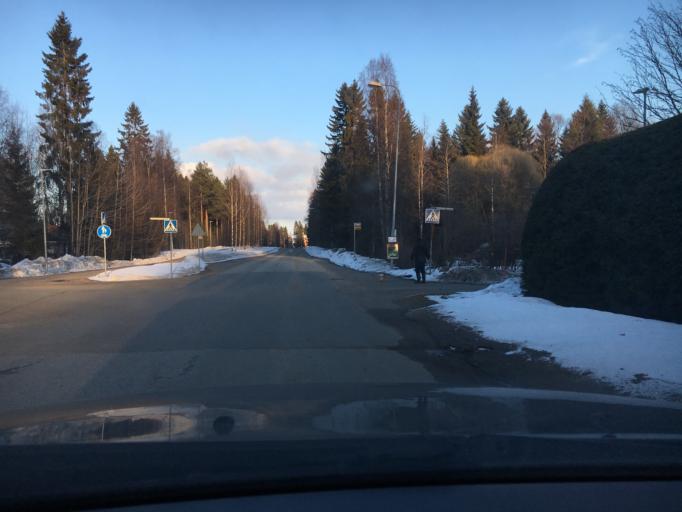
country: FI
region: Kainuu
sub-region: Kajaani
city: Kajaani
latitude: 64.2310
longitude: 27.7460
